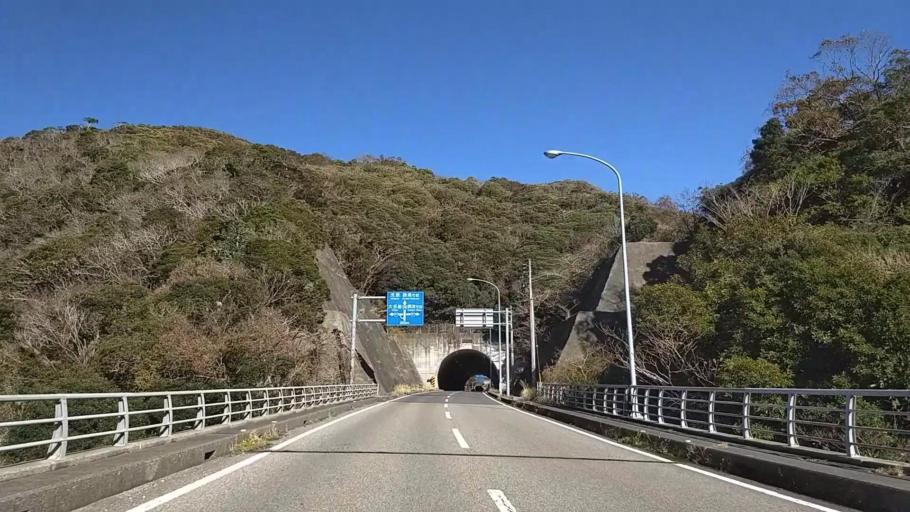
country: JP
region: Chiba
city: Katsuura
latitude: 35.1355
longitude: 140.2423
